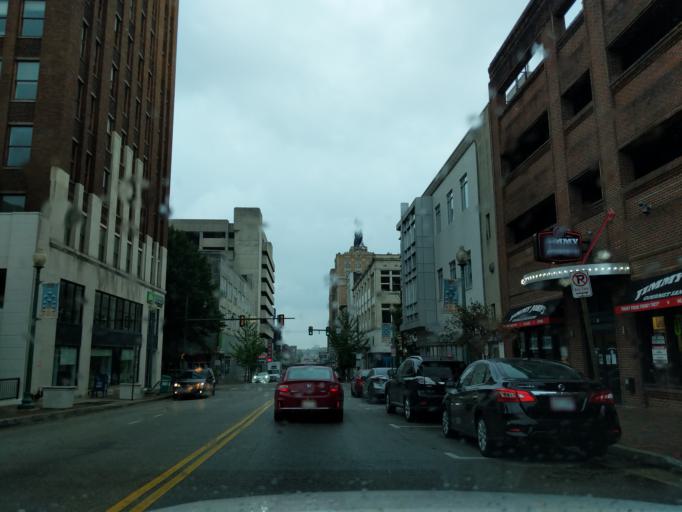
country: US
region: Tennessee
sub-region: Shelby County
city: Memphis
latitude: 35.1434
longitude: -90.0543
